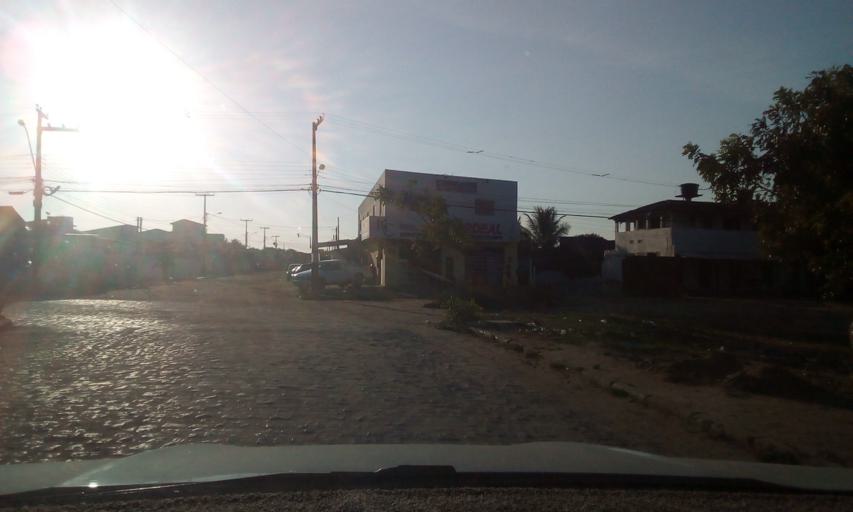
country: BR
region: Paraiba
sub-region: Bayeux
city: Bayeux
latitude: -7.1761
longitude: -34.9322
